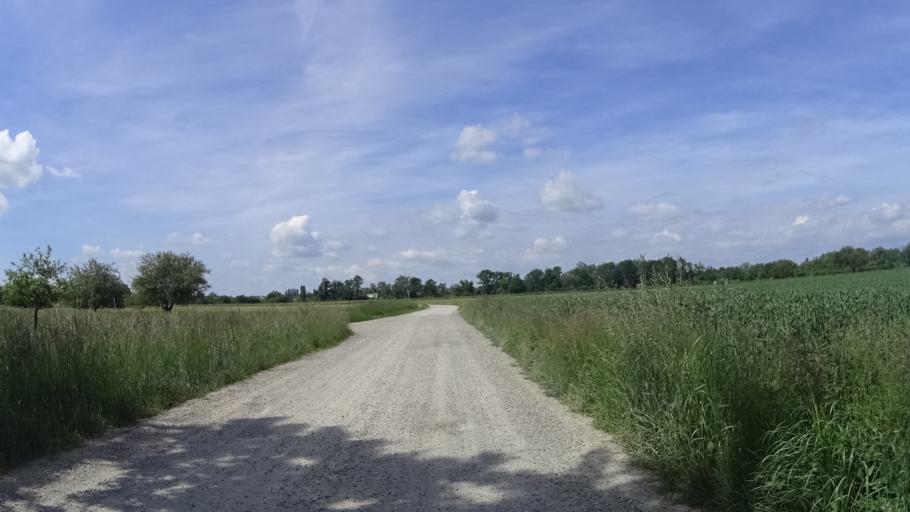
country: DE
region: Baden-Wuerttemberg
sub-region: Freiburg Region
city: Meissenheim
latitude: 48.4208
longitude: 7.7806
